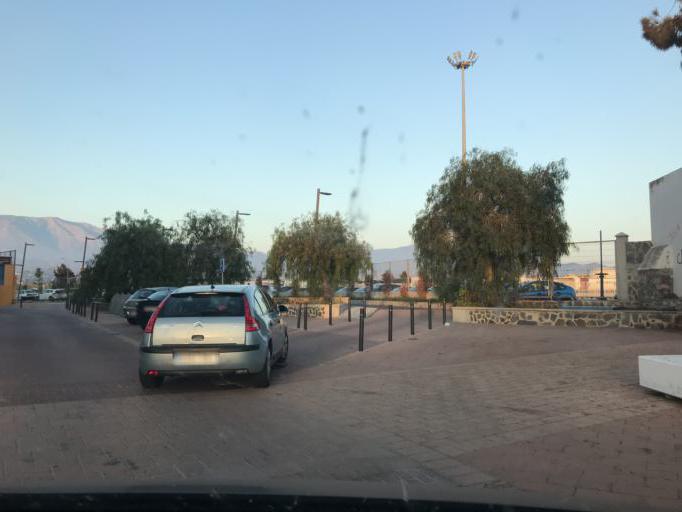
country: ES
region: Andalusia
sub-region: Provincia de Granada
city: El Varadero
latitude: 36.7224
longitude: -3.5201
